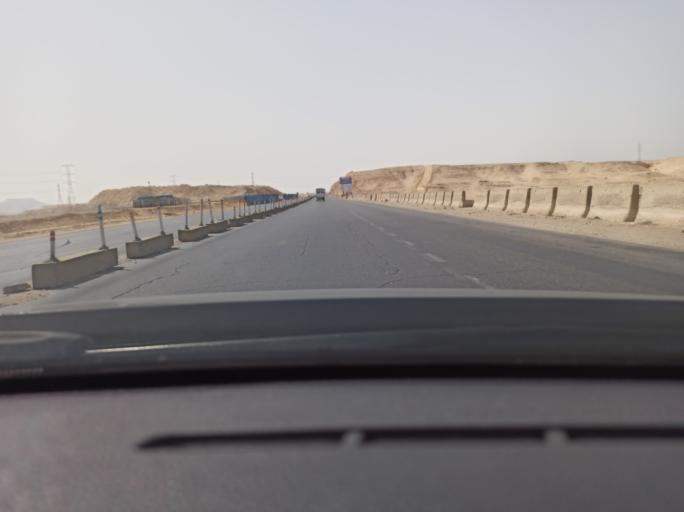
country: EG
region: Muhafazat Bani Suwayf
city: Bush
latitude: 29.1550
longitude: 31.2348
